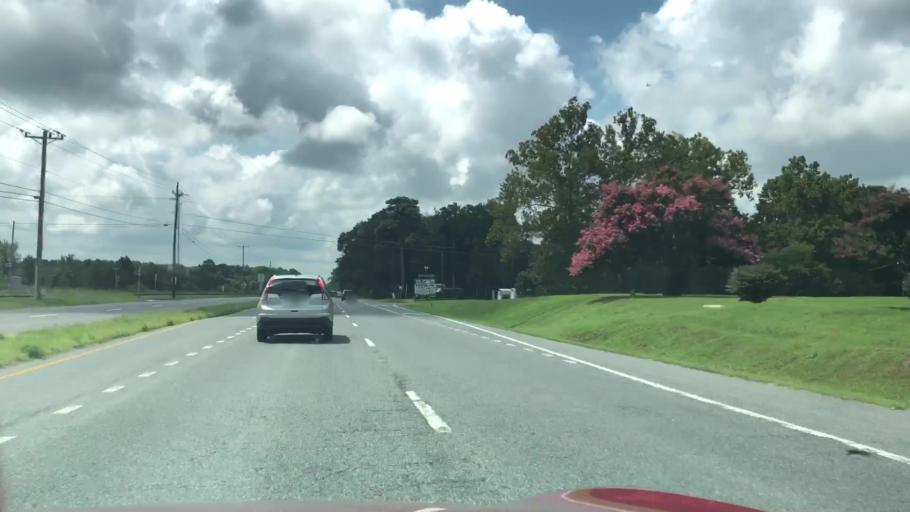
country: US
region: Virginia
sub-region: Northampton County
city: Eastville
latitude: 37.4391
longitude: -75.8824
